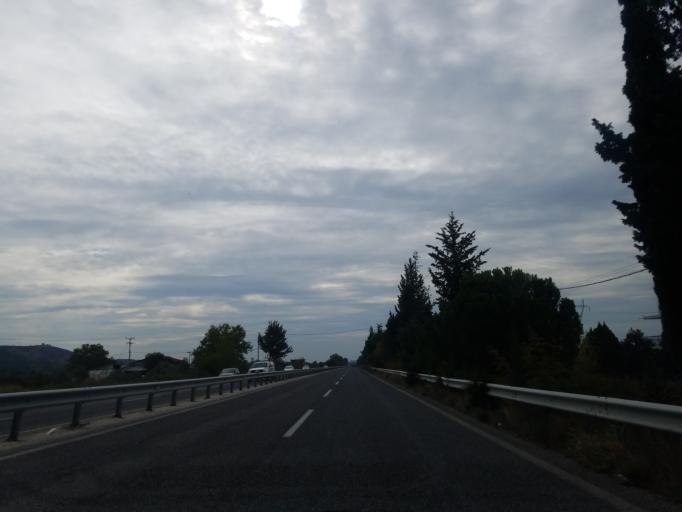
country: GR
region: Thessaly
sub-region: Trikala
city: Vasiliki
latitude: 39.6436
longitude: 21.6909
